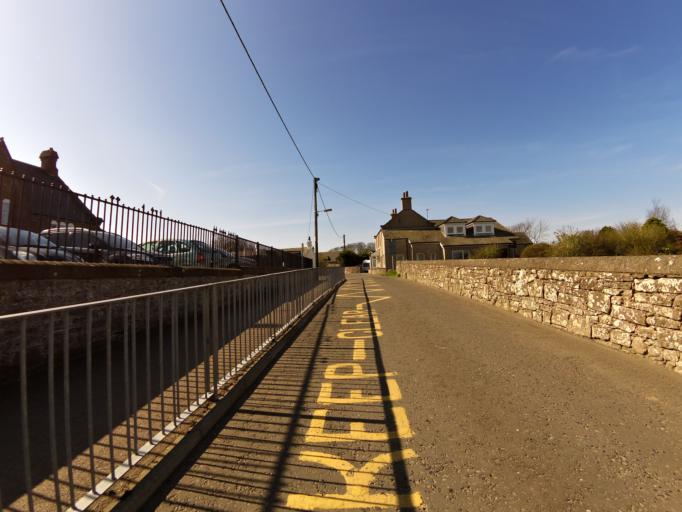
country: GB
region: Scotland
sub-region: Aberdeenshire
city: Laurencekirk
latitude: 56.7737
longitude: -2.4115
